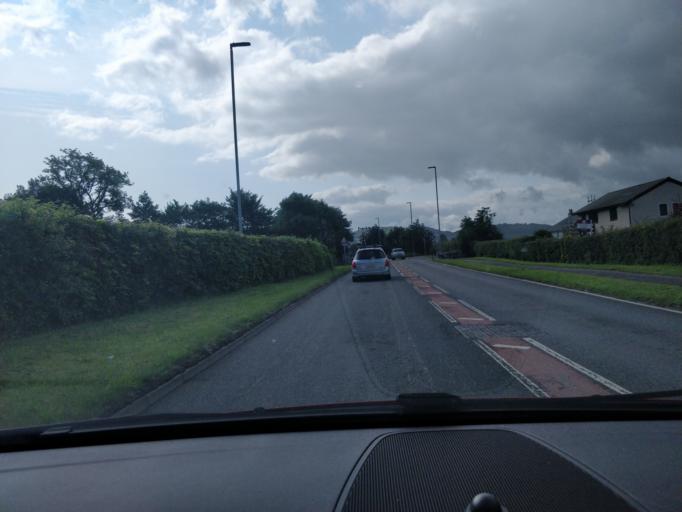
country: GB
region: Wales
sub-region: Conwy
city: Llanrwst
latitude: 53.1324
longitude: -3.7901
